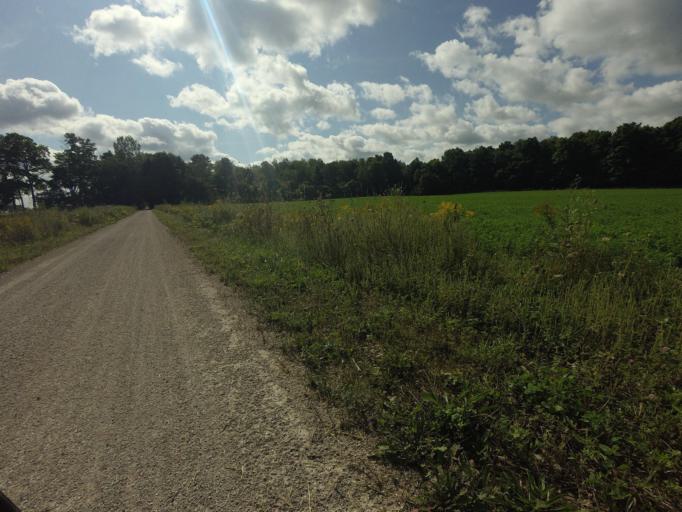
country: CA
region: Ontario
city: Huron East
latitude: 43.7134
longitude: -81.3801
